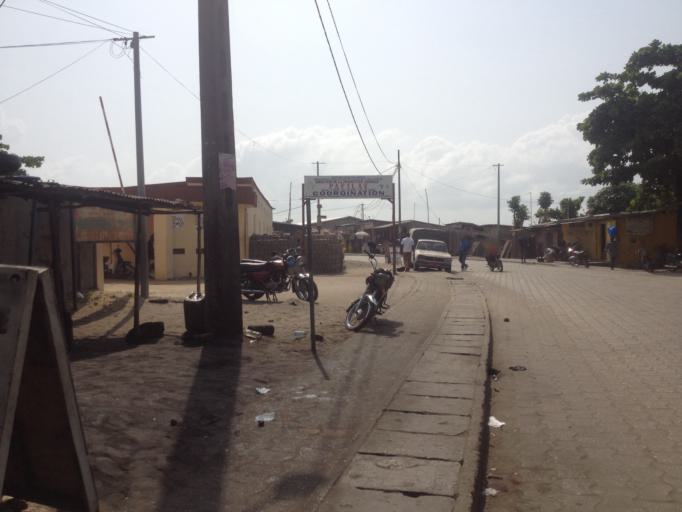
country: BJ
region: Littoral
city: Cotonou
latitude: 6.3588
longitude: 2.4455
